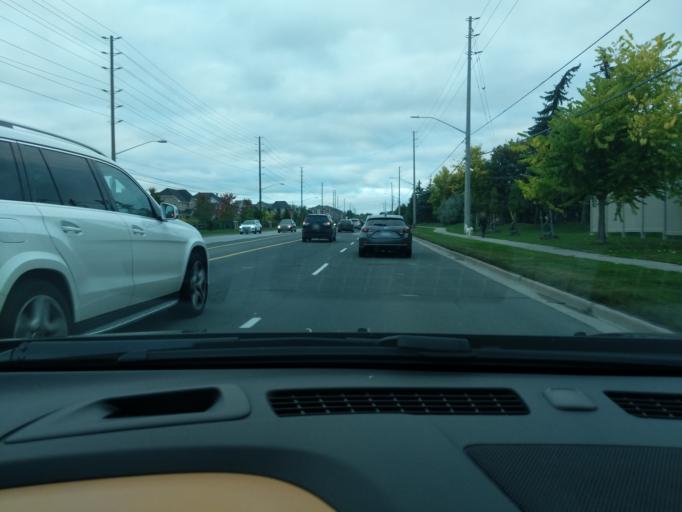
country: CA
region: Ontario
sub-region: York
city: Richmond Hill
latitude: 43.8786
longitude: -79.4660
